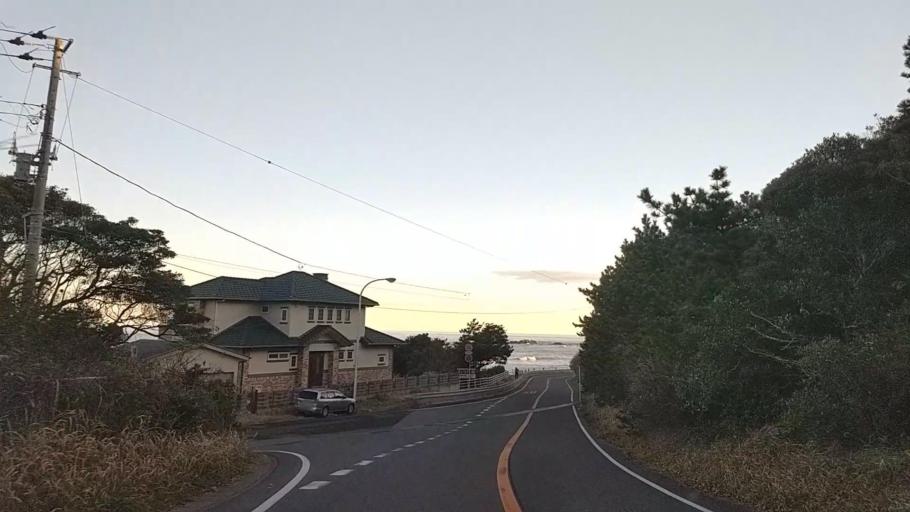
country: JP
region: Chiba
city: Hasaki
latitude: 35.7034
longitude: 140.8619
